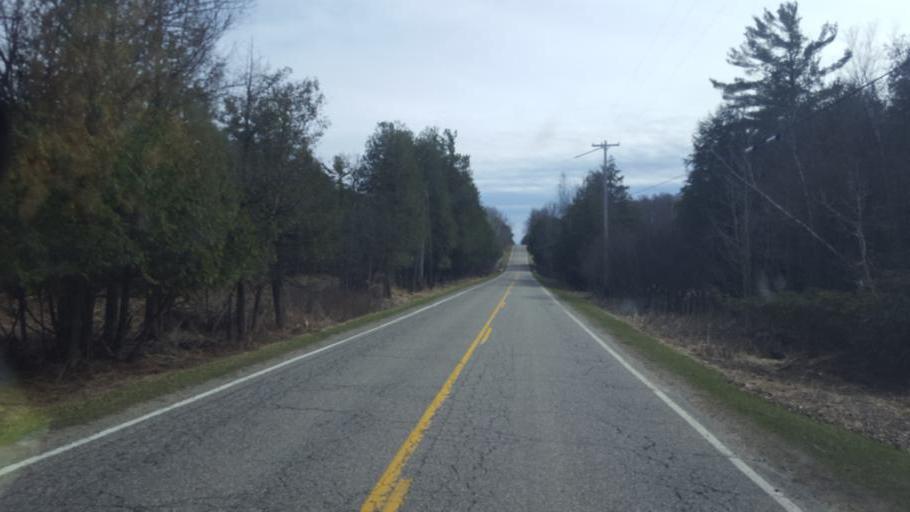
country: US
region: Michigan
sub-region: Montcalm County
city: Edmore
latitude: 43.4848
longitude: -85.0452
